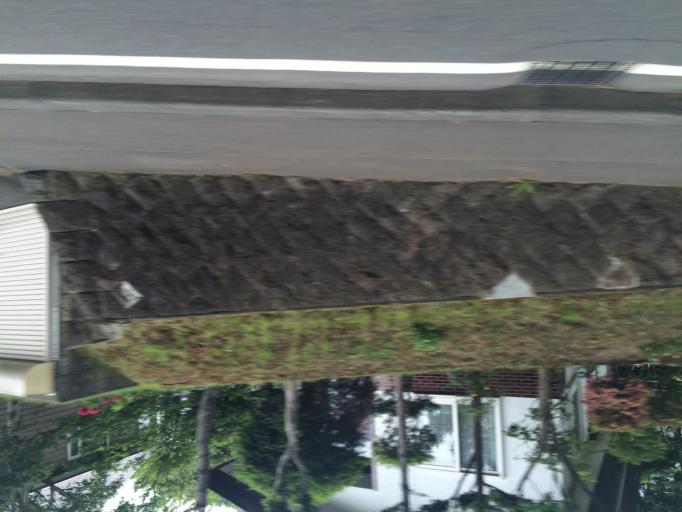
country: JP
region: Hokkaido
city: Sapporo
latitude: 43.0432
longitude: 141.2919
